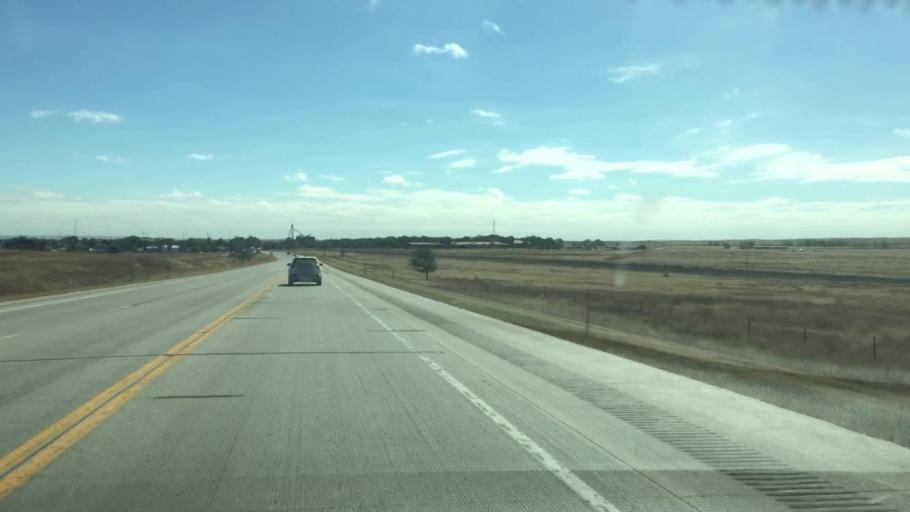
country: US
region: Colorado
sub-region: Lincoln County
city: Hugo
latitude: 39.1400
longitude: -103.4848
